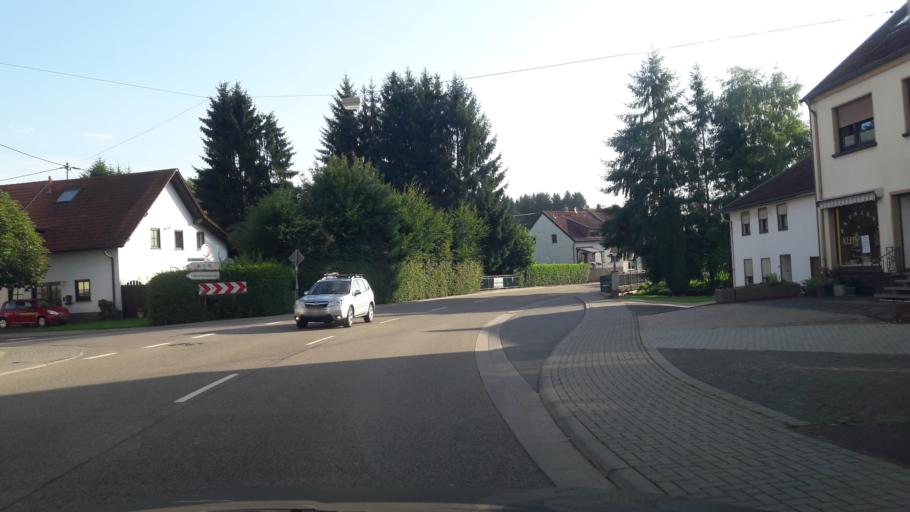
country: DE
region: Saarland
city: Eppelborn
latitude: 49.4338
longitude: 6.9497
